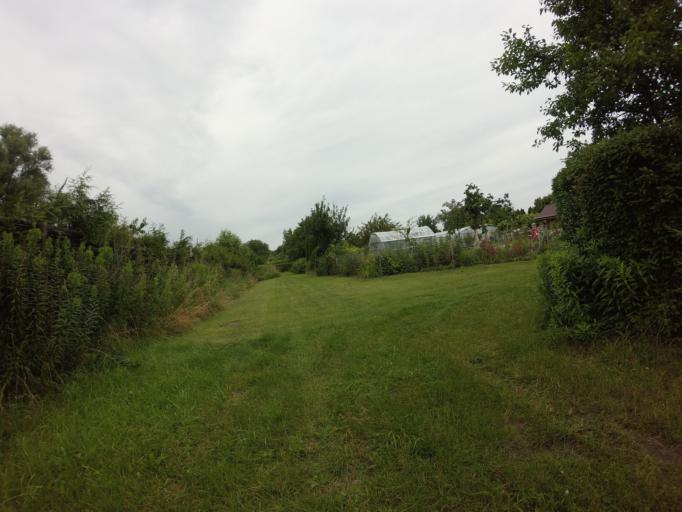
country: PL
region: West Pomeranian Voivodeship
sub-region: Powiat choszczenski
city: Choszczno
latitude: 53.1721
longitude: 15.4087
